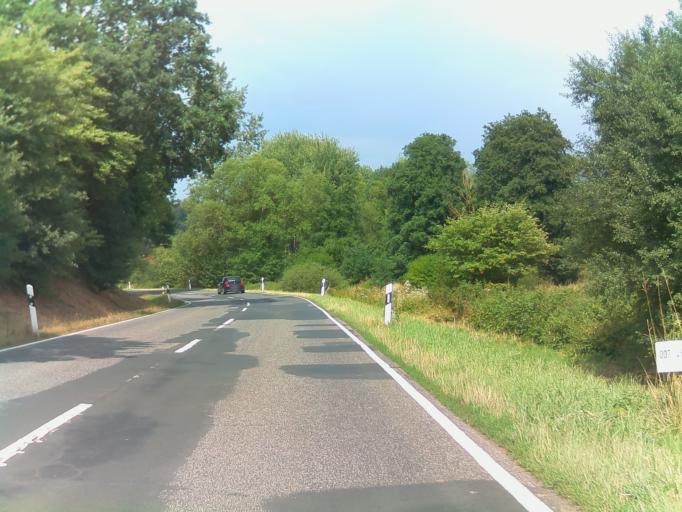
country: DE
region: Hesse
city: Grebenau
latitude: 50.7654
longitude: 9.5163
